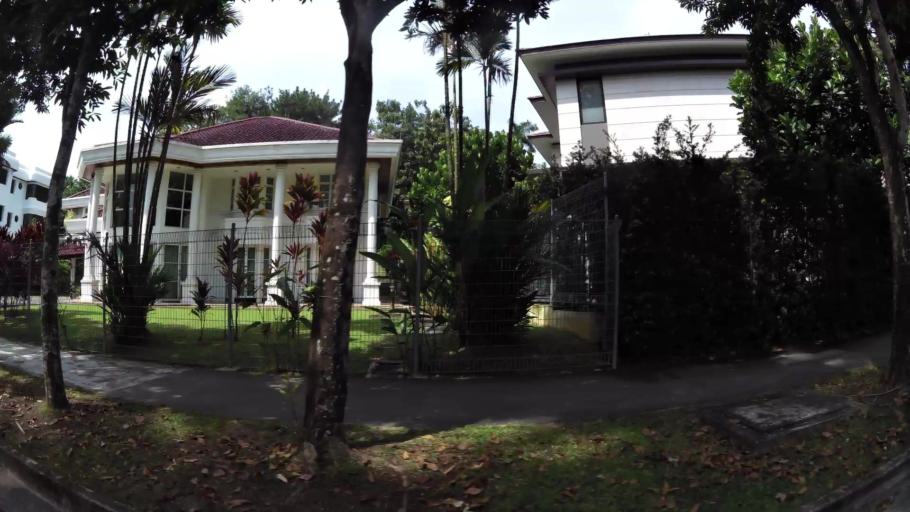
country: SG
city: Singapore
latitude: 1.3406
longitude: 103.7873
